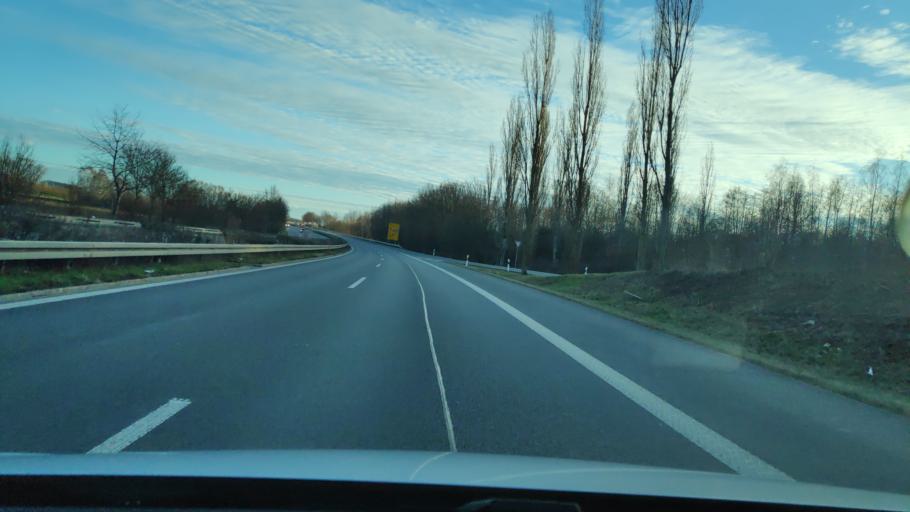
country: DE
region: Saxony
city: Zwickau
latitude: 50.7728
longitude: 12.4948
